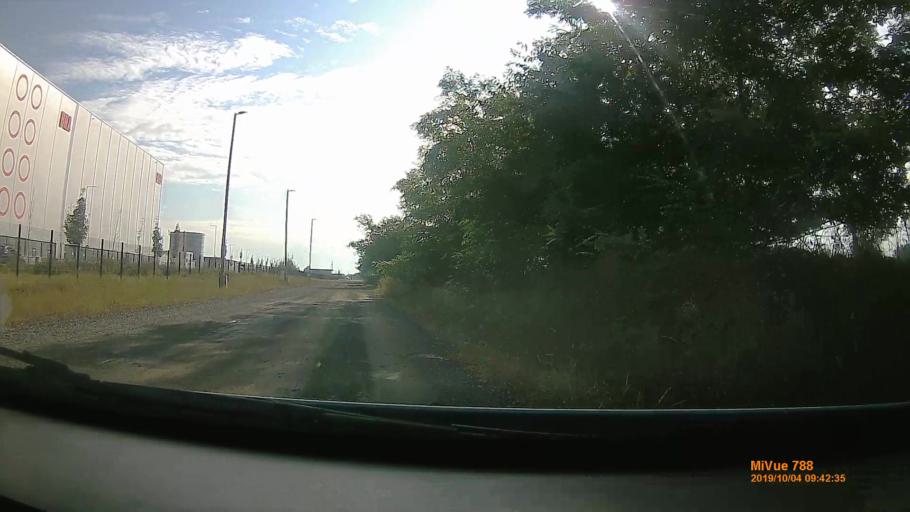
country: HU
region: Szabolcs-Szatmar-Bereg
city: Nyirtelek
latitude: 47.9481
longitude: 21.6430
